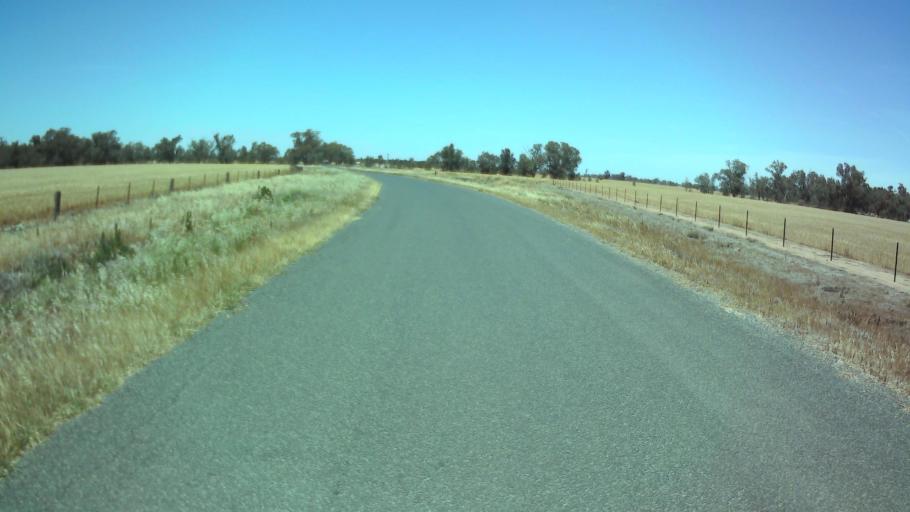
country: AU
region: New South Wales
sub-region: Weddin
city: Grenfell
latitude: -34.0355
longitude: 147.7897
